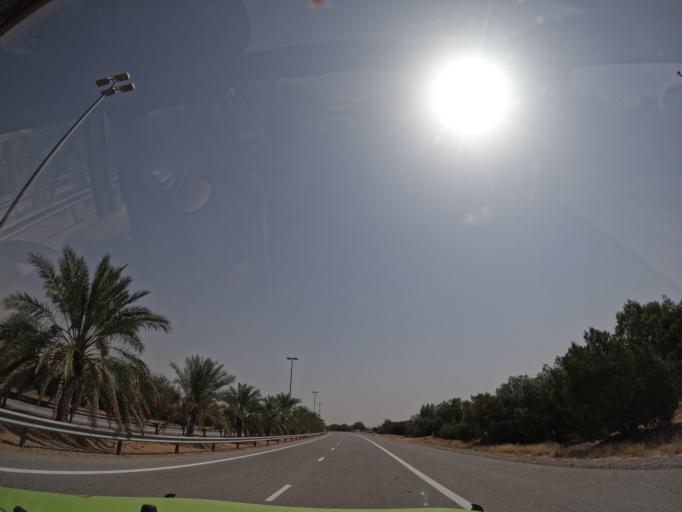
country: OM
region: Al Buraimi
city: Al Buraymi
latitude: 24.6842
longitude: 55.7155
